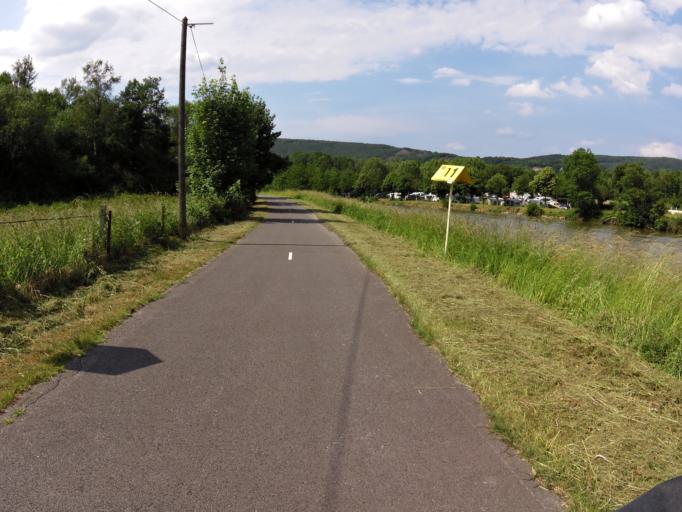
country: FR
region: Champagne-Ardenne
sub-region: Departement des Ardennes
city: Montherme
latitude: 49.8759
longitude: 4.7416
